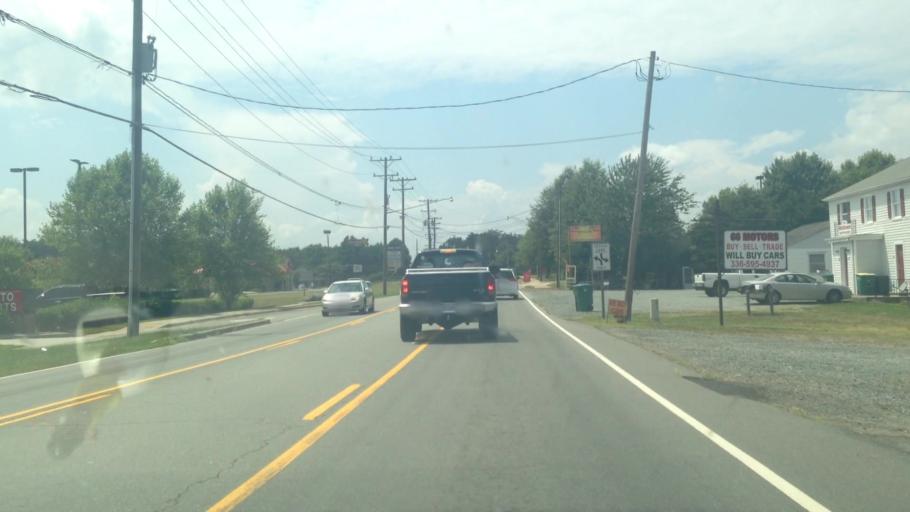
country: US
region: North Carolina
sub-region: Forsyth County
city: Walkertown
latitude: 36.1683
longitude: -80.1488
